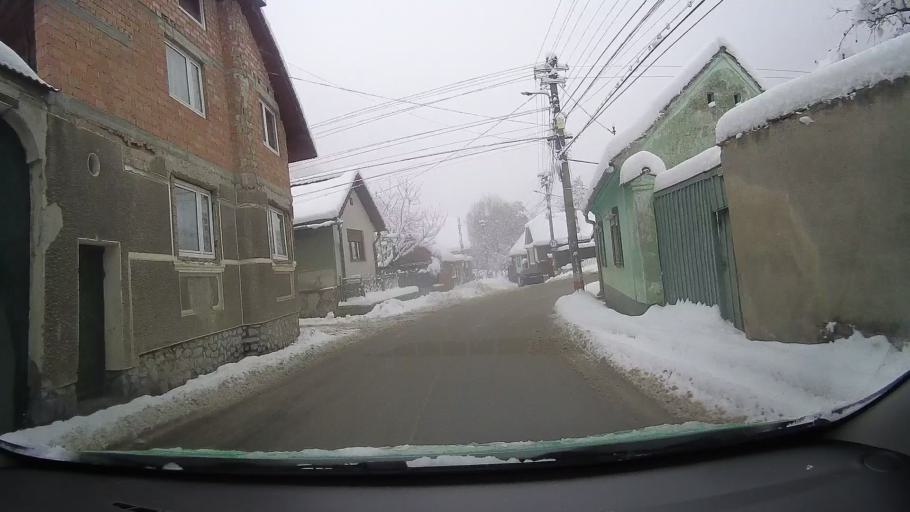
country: RO
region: Sibiu
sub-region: Comuna Tilisca
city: Tilisca
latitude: 45.7980
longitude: 23.8649
